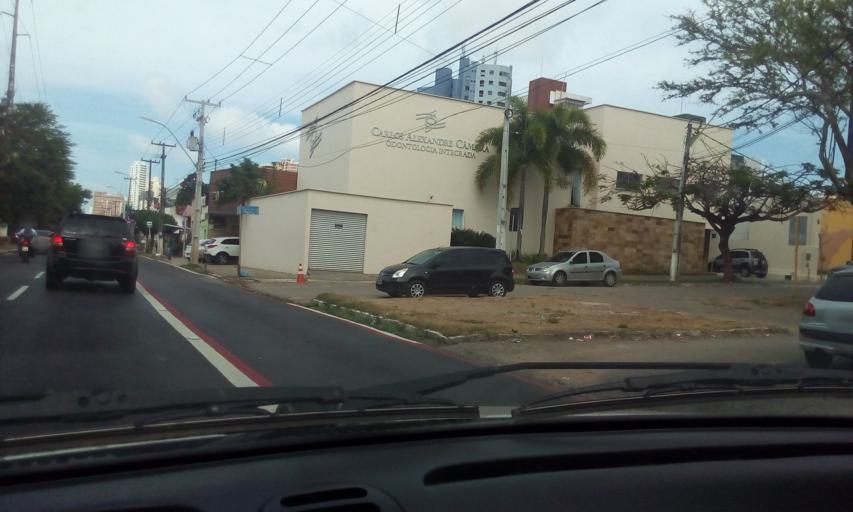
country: BR
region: Rio Grande do Norte
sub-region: Natal
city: Natal
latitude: -5.7997
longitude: -35.2056
